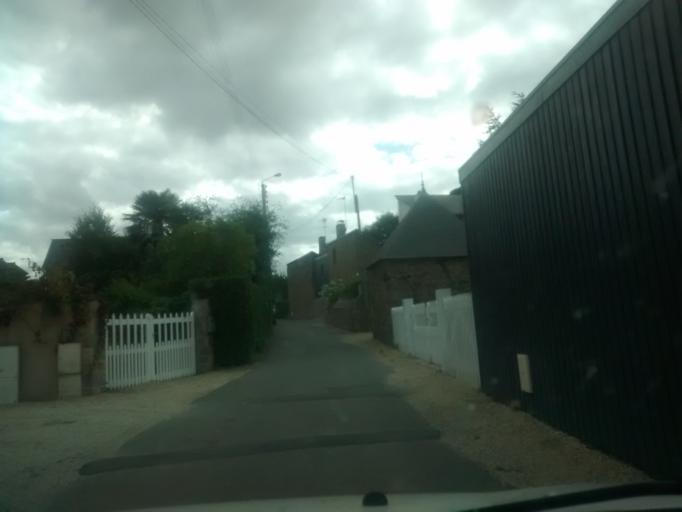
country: FR
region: Brittany
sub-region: Departement d'Ille-et-Vilaine
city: Saint-Briac-sur-Mer
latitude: 48.6234
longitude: -2.1347
